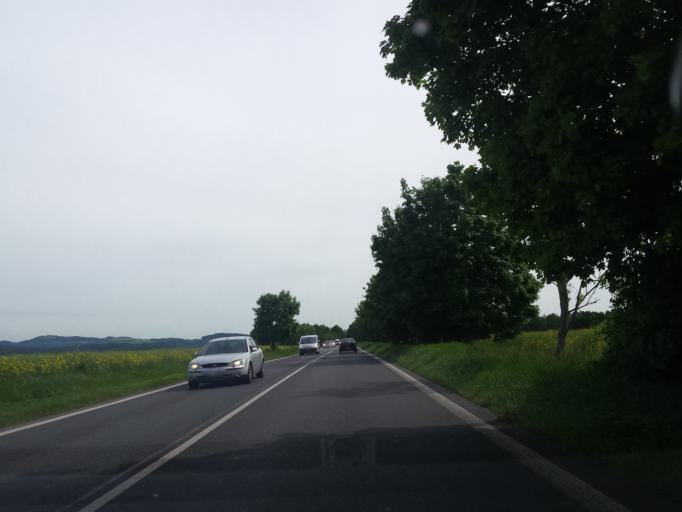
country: CZ
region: Liberecky
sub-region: Okres Ceska Lipa
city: Ceska Lipa
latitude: 50.6418
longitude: 14.5362
